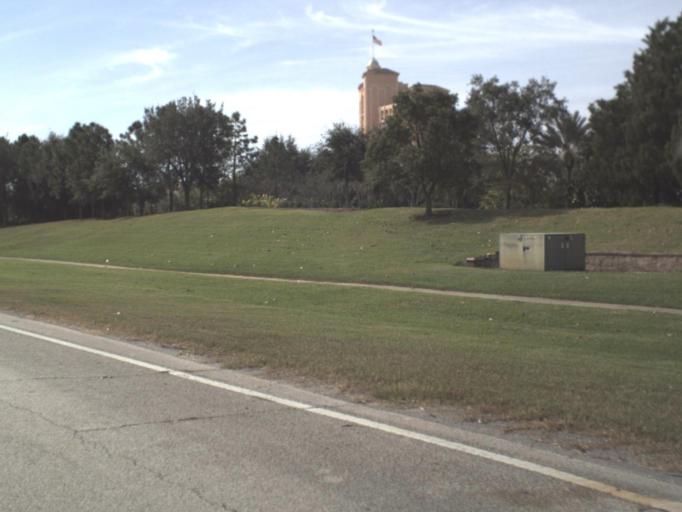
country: US
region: Florida
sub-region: Orange County
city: Williamsburg
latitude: 28.4056
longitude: -81.4253
